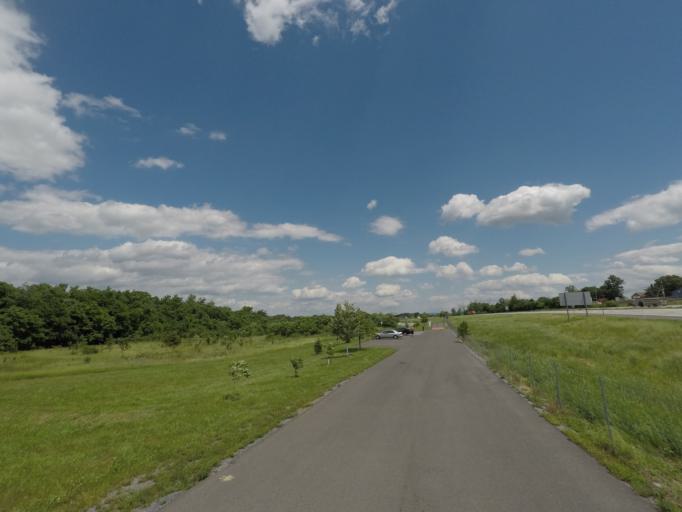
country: US
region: West Virginia
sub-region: Berkeley County
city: Martinsburg
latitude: 39.4335
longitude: -77.9563
